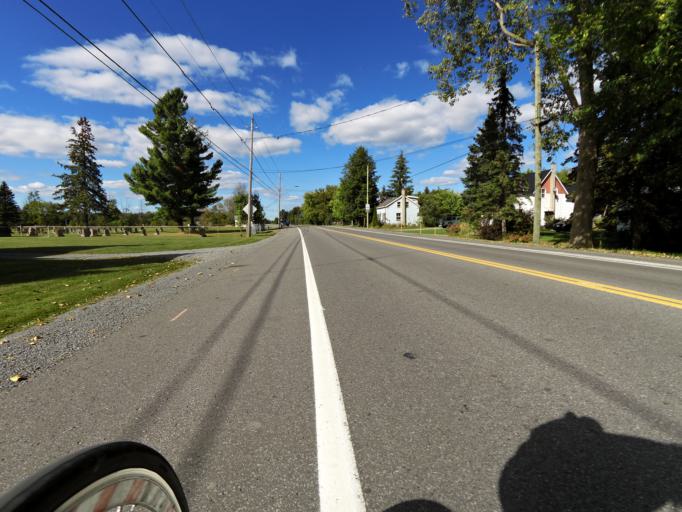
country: CA
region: Ontario
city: Bells Corners
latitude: 45.1546
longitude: -75.6490
